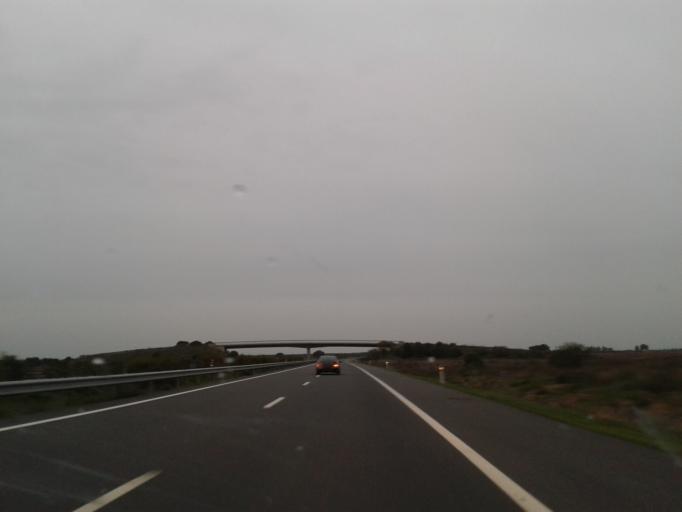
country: PT
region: Beja
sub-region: Aljustrel
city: Aljustrel
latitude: 37.9864
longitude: -8.2629
